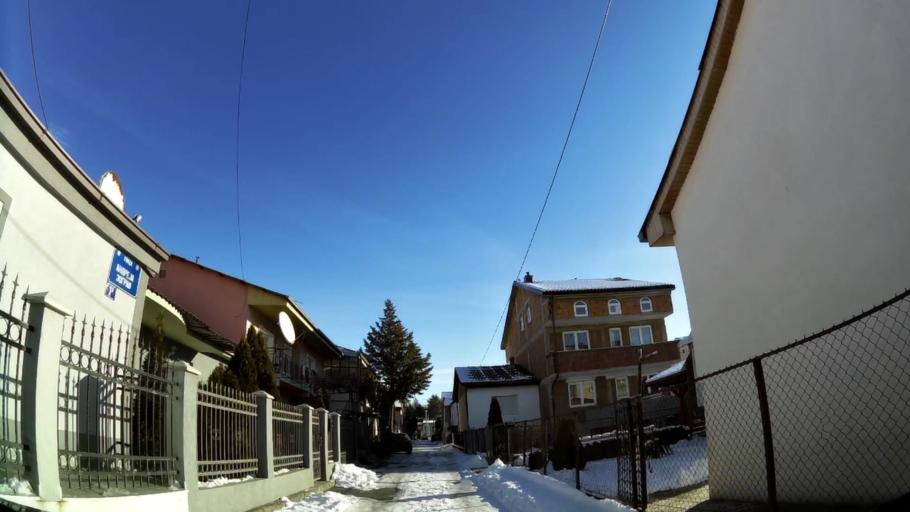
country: MK
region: Saraj
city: Saraj
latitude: 42.0075
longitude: 21.3344
